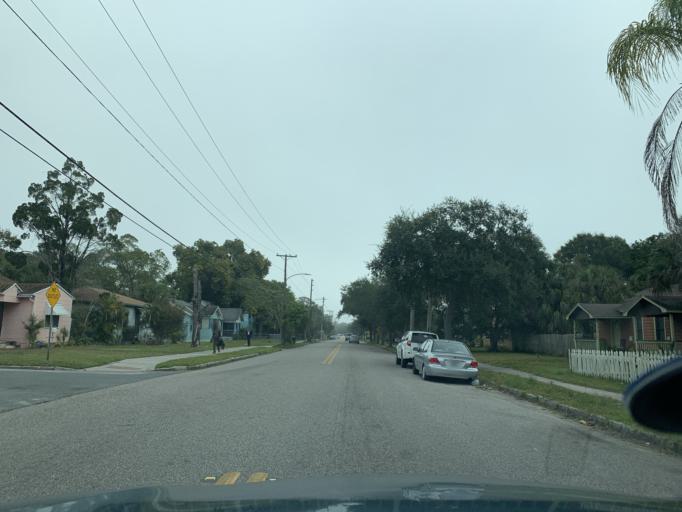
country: US
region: Florida
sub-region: Pinellas County
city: Saint Petersburg
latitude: 27.7521
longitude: -82.6439
